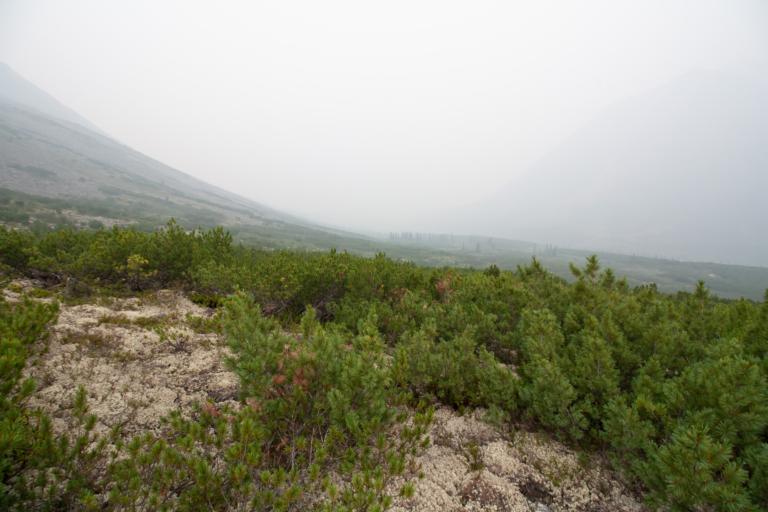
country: RU
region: Respublika Buryatiya
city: Kichera
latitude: 56.2390
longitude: 110.6015
